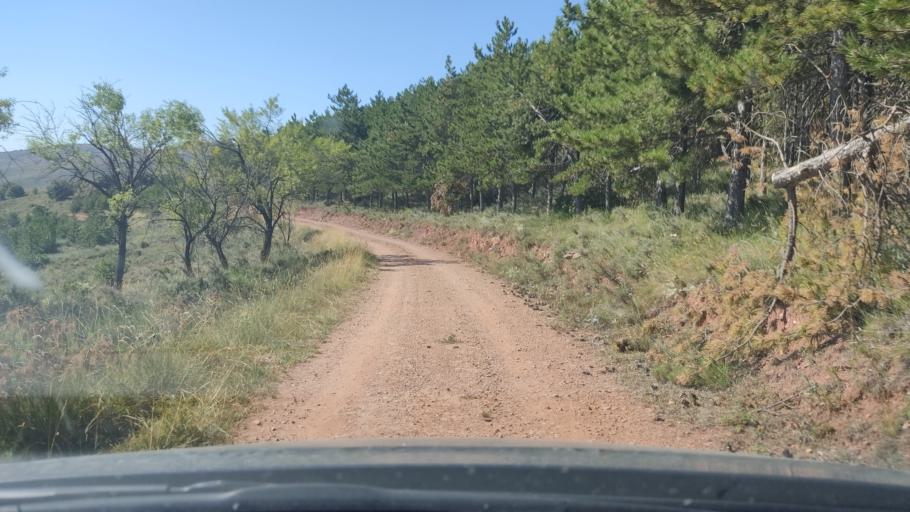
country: ES
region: Aragon
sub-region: Provincia de Teruel
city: Monforte de Moyuela
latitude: 41.0436
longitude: -1.0356
